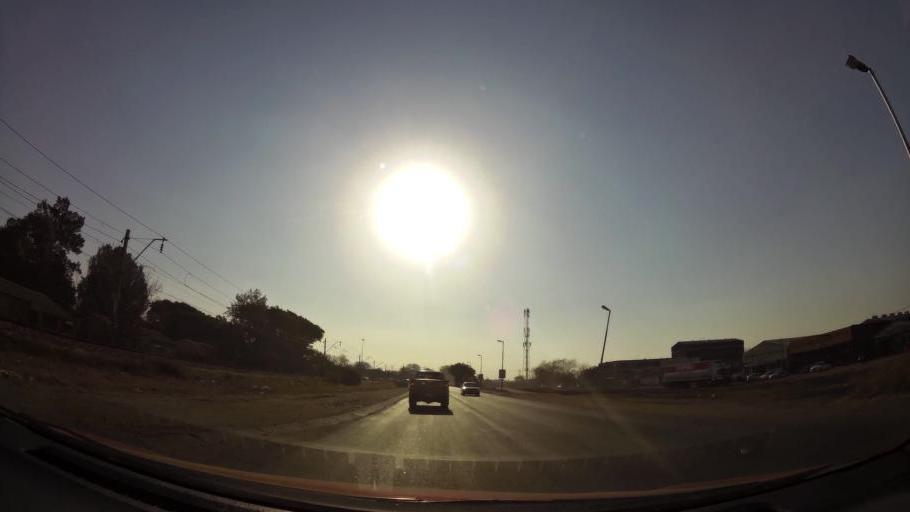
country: ZA
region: North-West
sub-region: Bojanala Platinum District Municipality
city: Rustenburg
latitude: -25.6452
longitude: 27.2324
